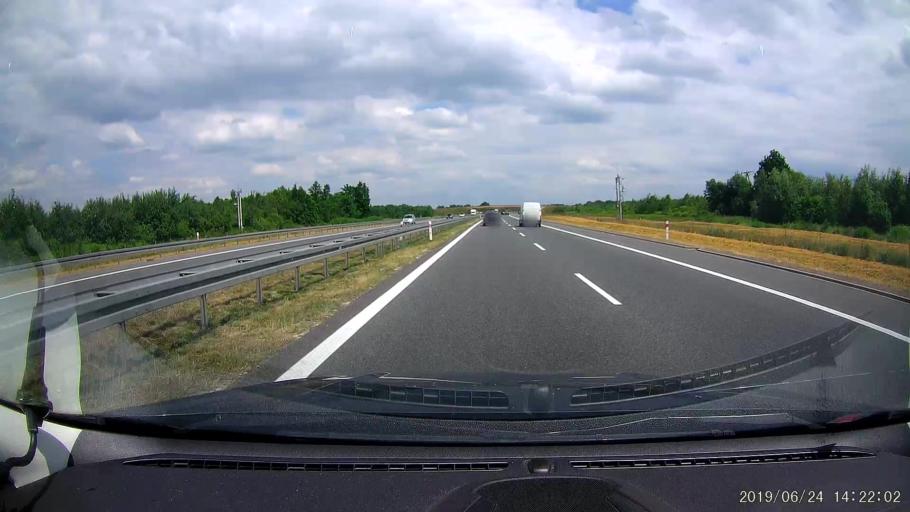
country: PL
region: Lesser Poland Voivodeship
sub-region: Powiat bochenski
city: Krzeczow
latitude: 50.0060
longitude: 20.4948
